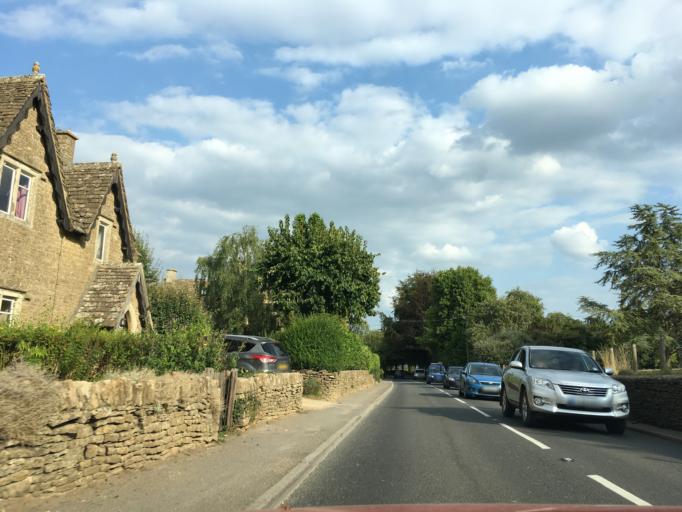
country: GB
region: England
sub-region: Gloucestershire
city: Tetbury
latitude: 51.6427
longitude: -2.2003
